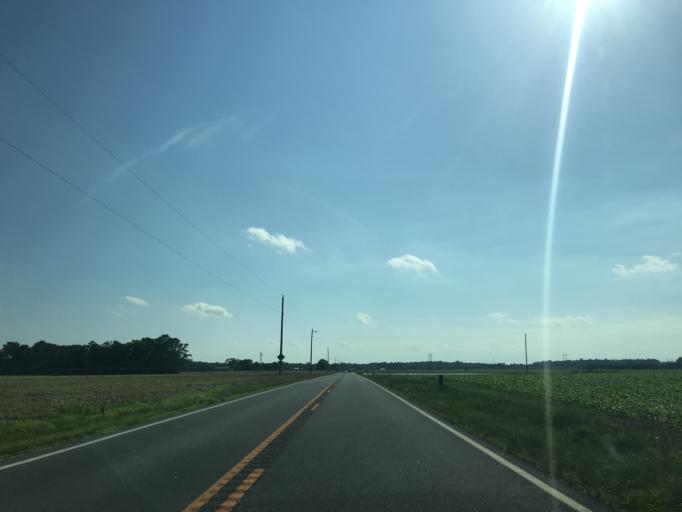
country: US
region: Maryland
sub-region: Wicomico County
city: Hebron
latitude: 38.4653
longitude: -75.6746
